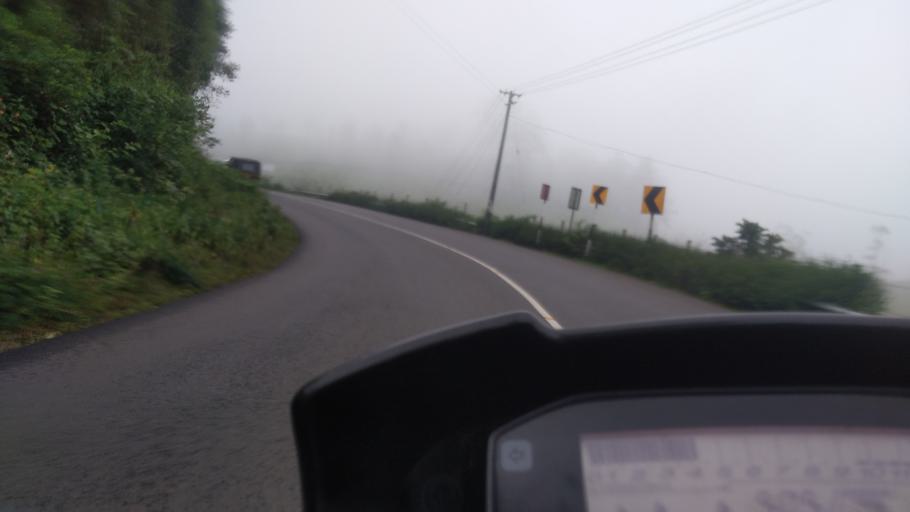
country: IN
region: Tamil Nadu
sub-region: Theni
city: Gudalur
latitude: 9.5799
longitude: 77.0385
